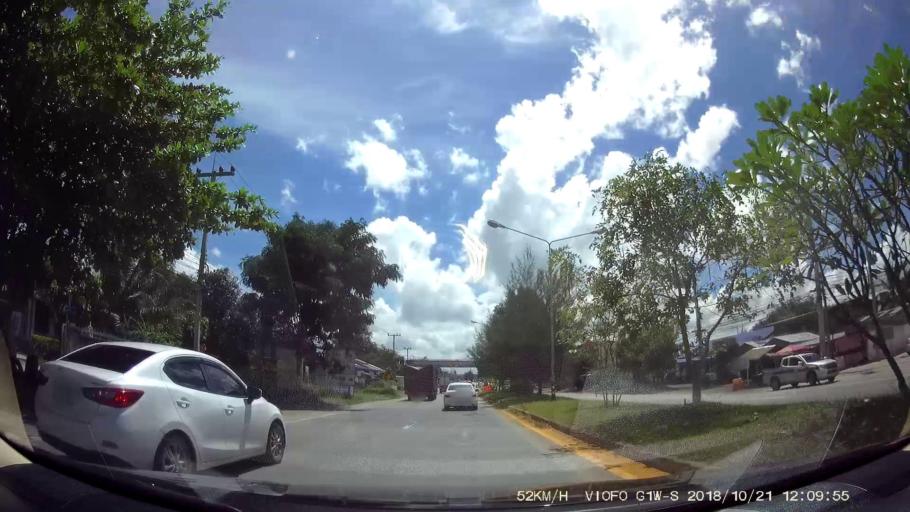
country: TH
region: Chaiyaphum
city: Chatturat
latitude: 15.4159
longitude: 101.8333
